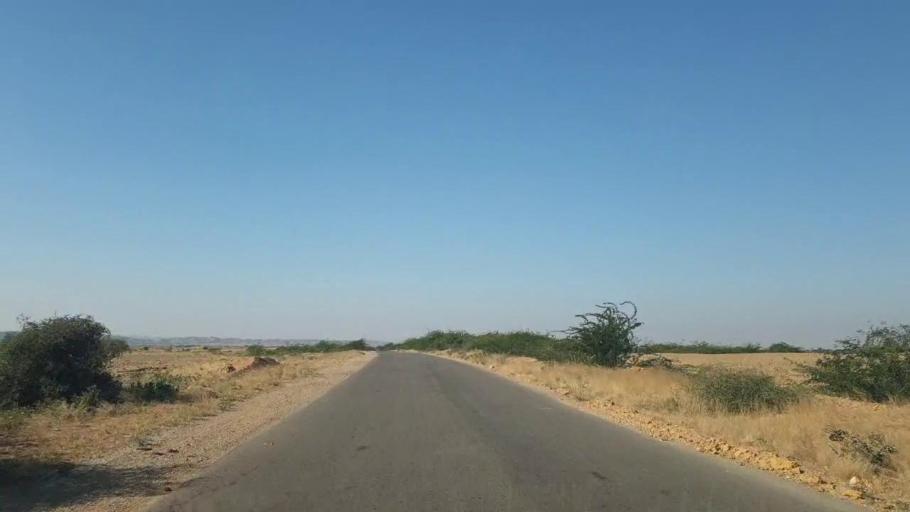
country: PK
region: Sindh
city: Malir Cantonment
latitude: 25.2699
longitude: 67.5935
